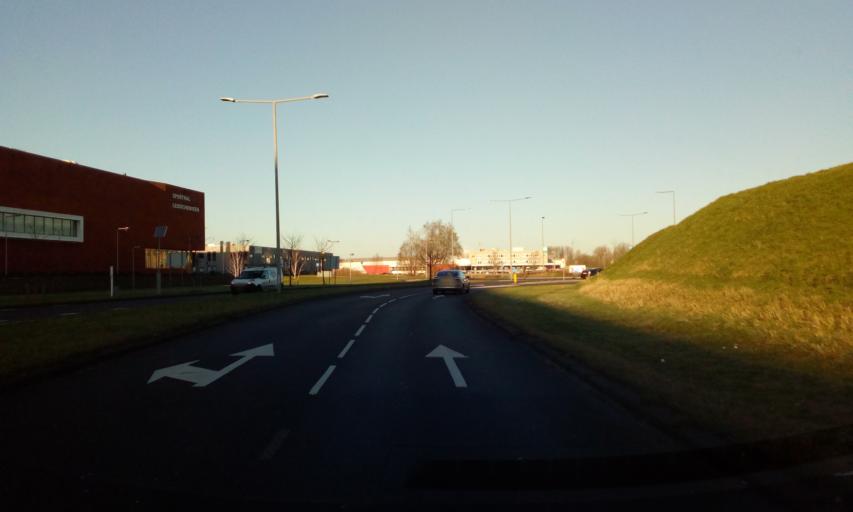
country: NL
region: South Holland
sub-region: Gemeente Den Haag
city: Ypenburg
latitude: 52.0671
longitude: 4.4001
